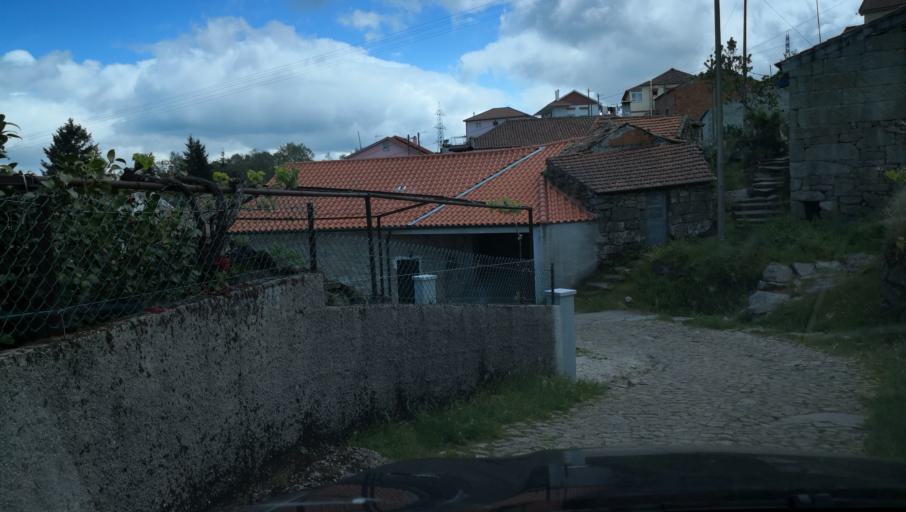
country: PT
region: Vila Real
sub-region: Vila Real
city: Vila Real
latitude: 41.4074
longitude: -7.7166
